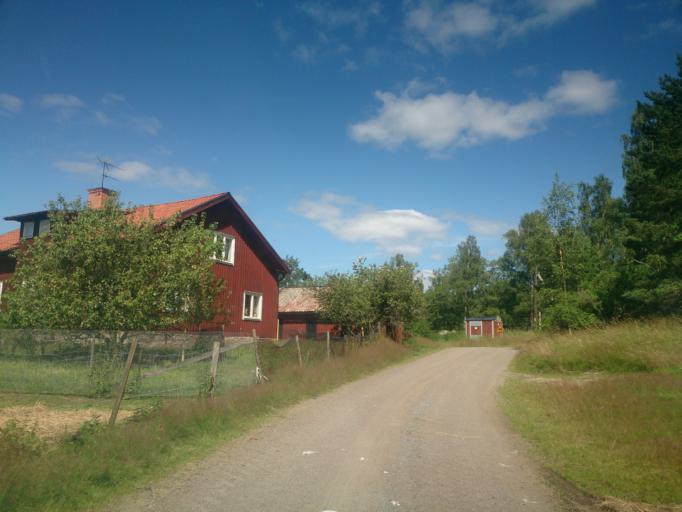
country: SE
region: OEstergoetland
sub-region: Atvidabergs Kommun
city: Atvidaberg
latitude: 58.2451
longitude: 16.0083
